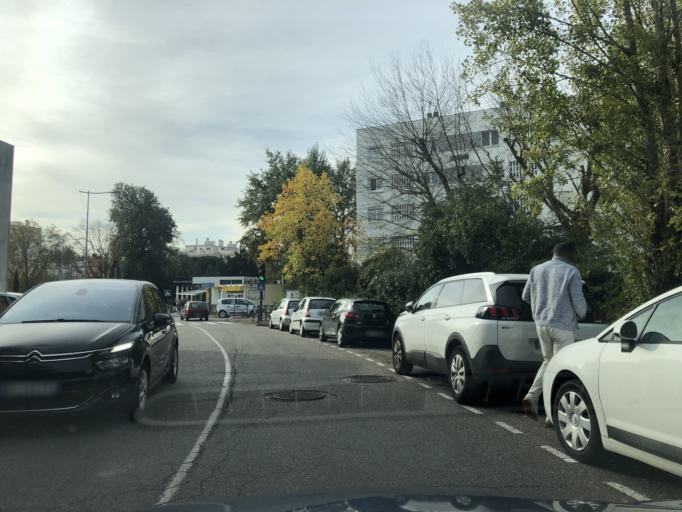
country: FR
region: Aquitaine
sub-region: Departement de la Gironde
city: Merignac
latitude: 44.8425
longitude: -0.6510
